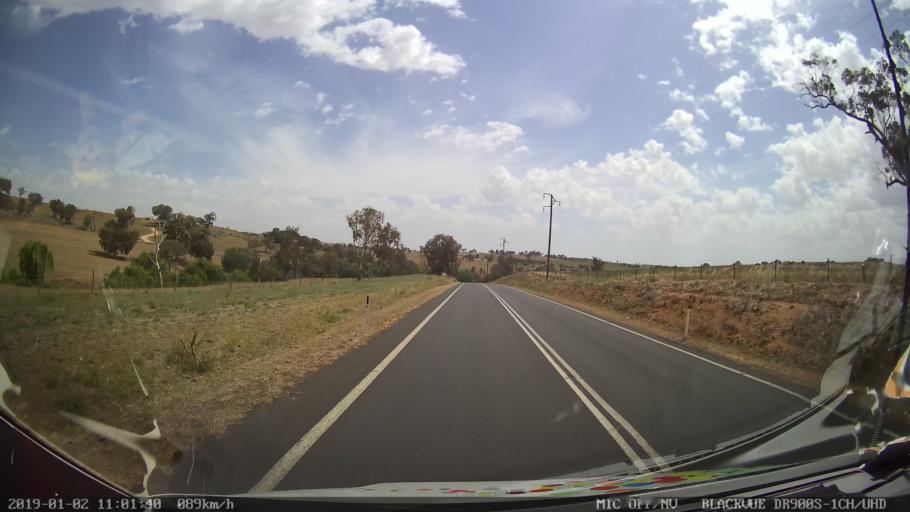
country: AU
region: New South Wales
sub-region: Young
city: Young
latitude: -34.5954
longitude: 148.3214
